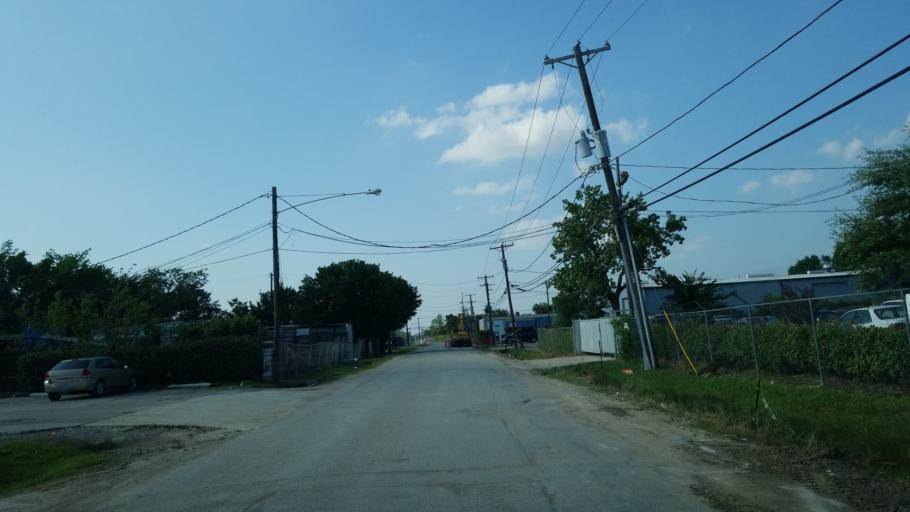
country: US
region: Texas
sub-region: Dallas County
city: Farmers Branch
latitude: 32.8904
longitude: -96.9019
